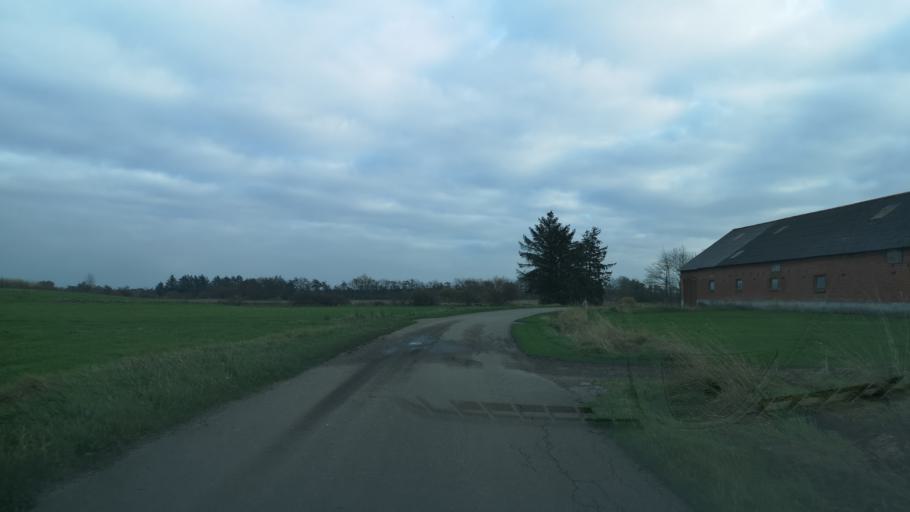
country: DK
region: Central Jutland
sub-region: Ringkobing-Skjern Kommune
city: Videbaek
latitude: 56.0342
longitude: 8.5959
